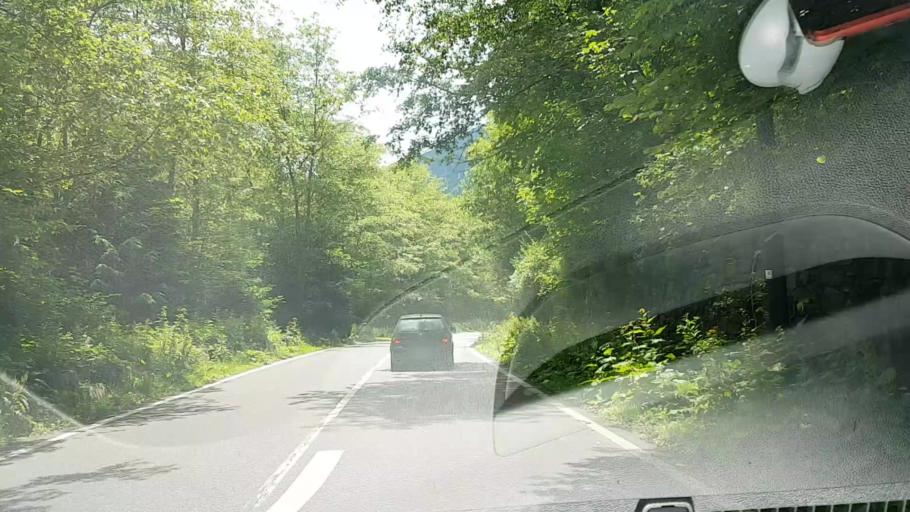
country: RO
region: Suceava
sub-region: Comuna Crucea
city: Crucea
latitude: 47.2967
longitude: 25.6323
